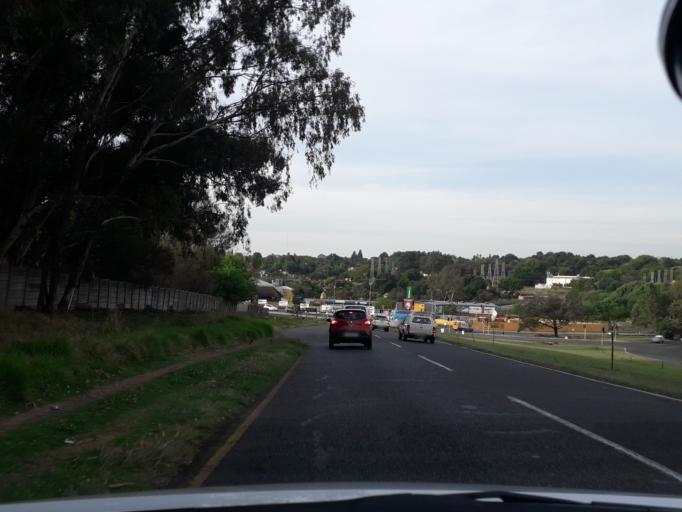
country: ZA
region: Gauteng
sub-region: City of Johannesburg Metropolitan Municipality
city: Modderfontein
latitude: -26.1297
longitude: 28.1194
